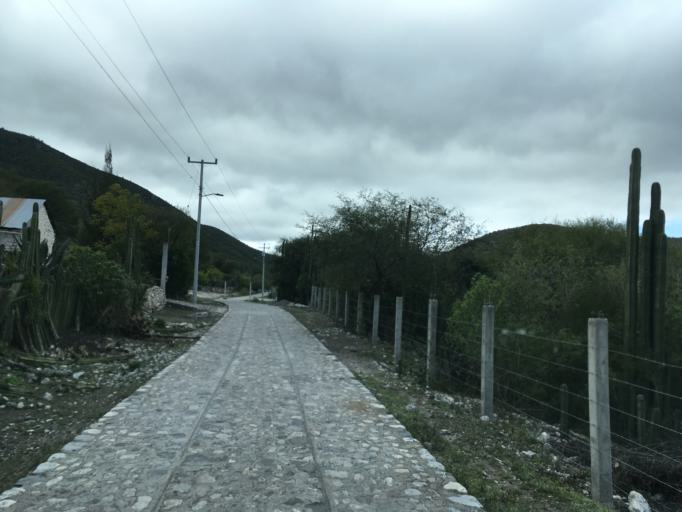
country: MX
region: Hidalgo
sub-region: Metztitlan
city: Fontezuelas
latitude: 20.6244
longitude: -98.8605
